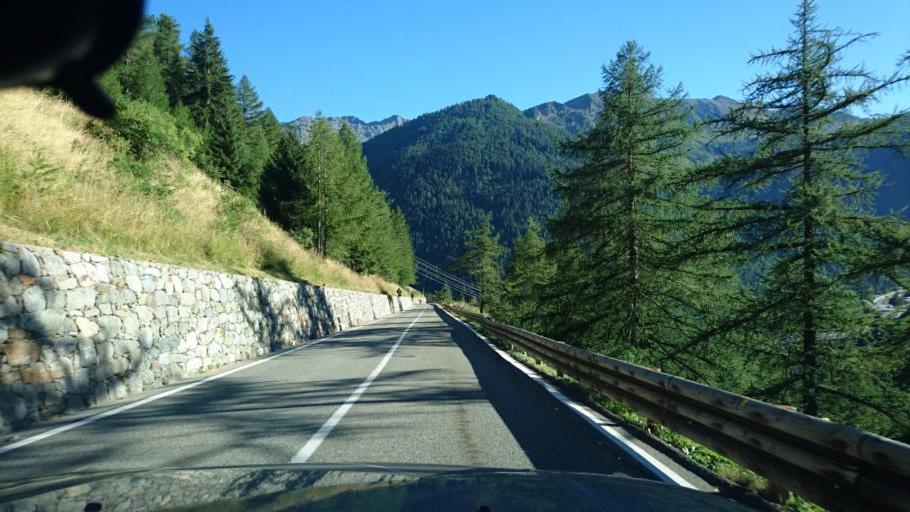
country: IT
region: Aosta Valley
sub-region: Valle d'Aosta
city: San Leonardo
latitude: 45.8274
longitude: 7.1883
